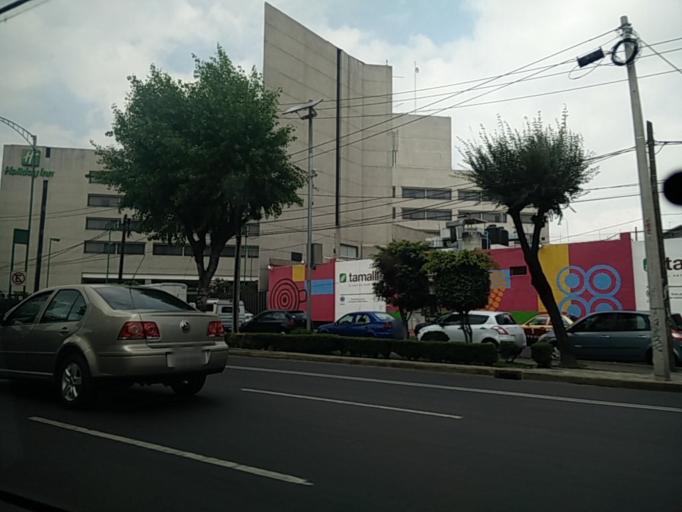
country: MX
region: Mexico City
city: Colonia del Valle
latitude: 19.3684
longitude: -99.1618
